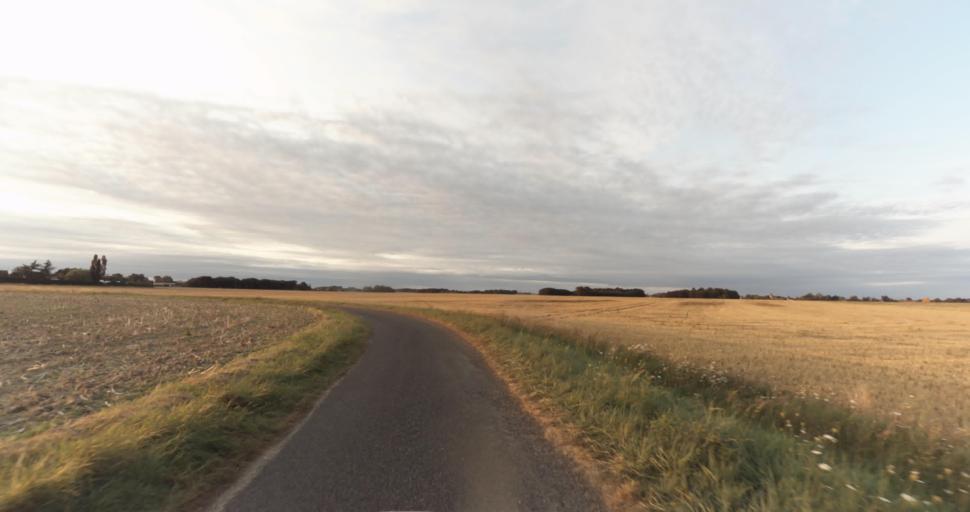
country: FR
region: Haute-Normandie
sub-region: Departement de l'Eure
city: La Madeleine-de-Nonancourt
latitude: 48.8665
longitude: 1.1893
